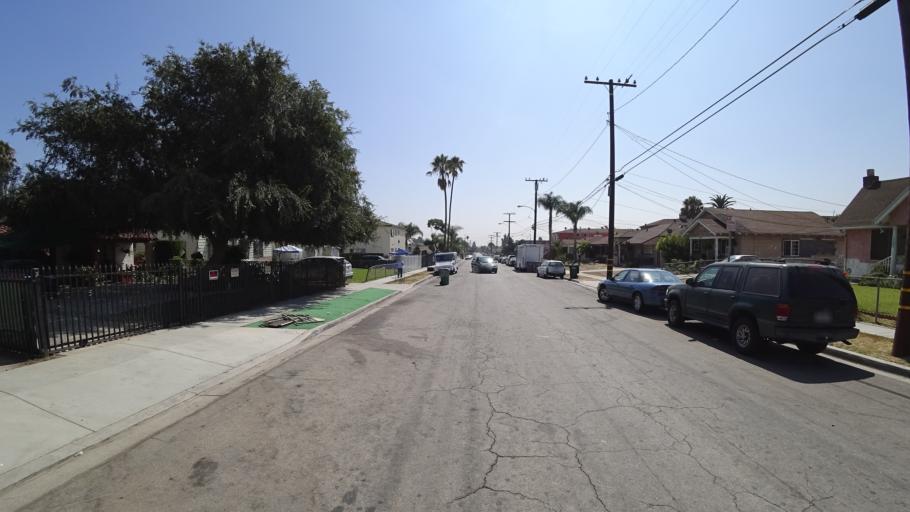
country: US
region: California
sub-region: Los Angeles County
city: Westmont
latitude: 33.9389
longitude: -118.2985
